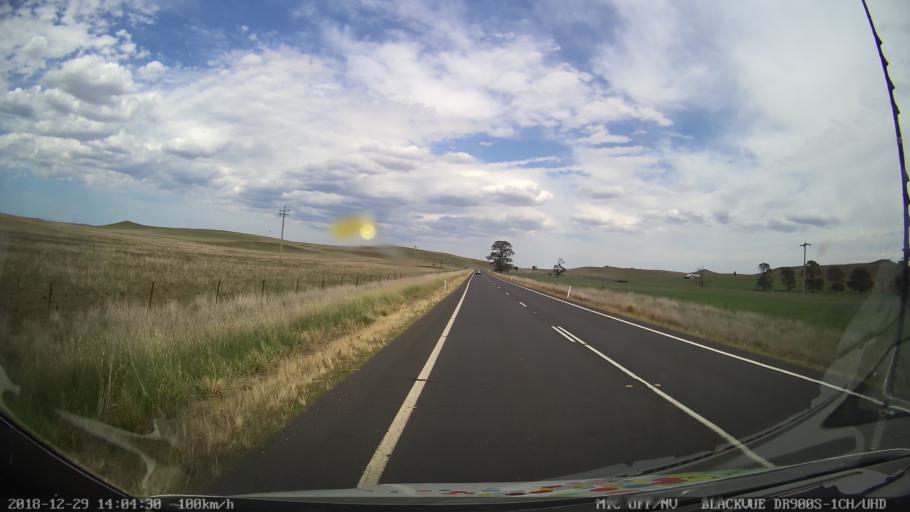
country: AU
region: New South Wales
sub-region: Cooma-Monaro
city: Cooma
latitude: -36.3171
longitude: 149.1870
